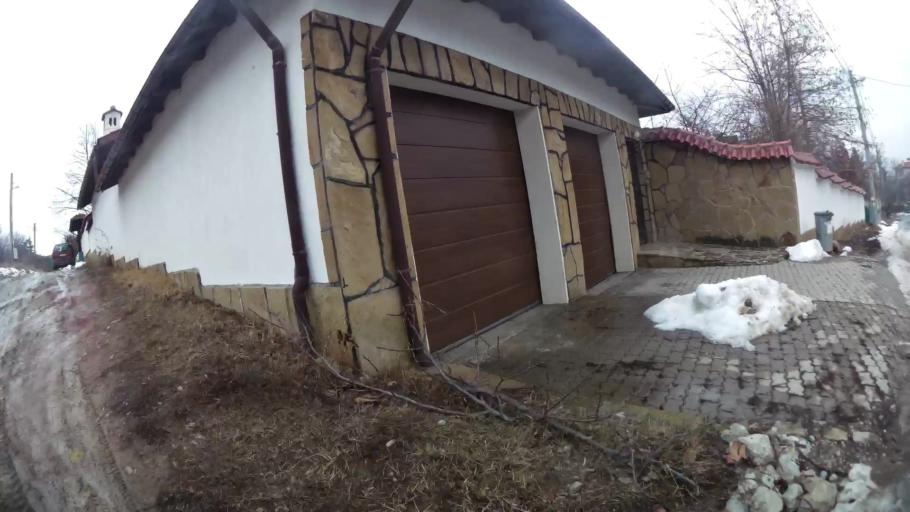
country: BG
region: Sofiya
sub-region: Obshtina Bozhurishte
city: Bozhurishte
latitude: 42.6709
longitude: 23.2284
